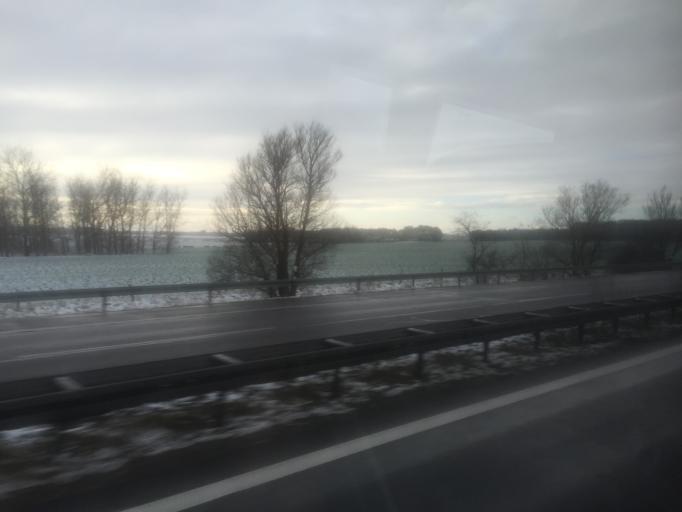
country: DE
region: Brandenburg
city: Fehrbellin
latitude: 52.7518
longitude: 12.8652
